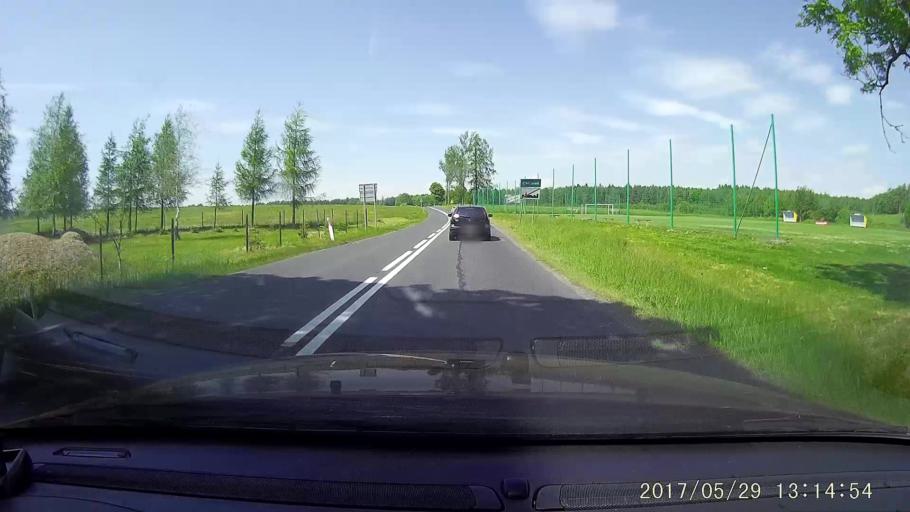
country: PL
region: Lower Silesian Voivodeship
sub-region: Powiat lwowecki
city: Lubomierz
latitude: 50.9824
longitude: 15.4854
